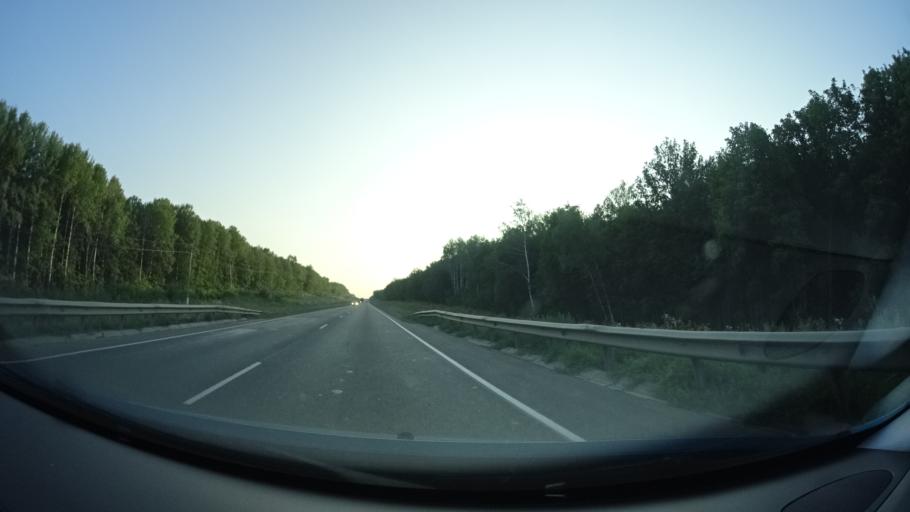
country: RU
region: Samara
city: Isakly
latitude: 54.0108
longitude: 51.6807
